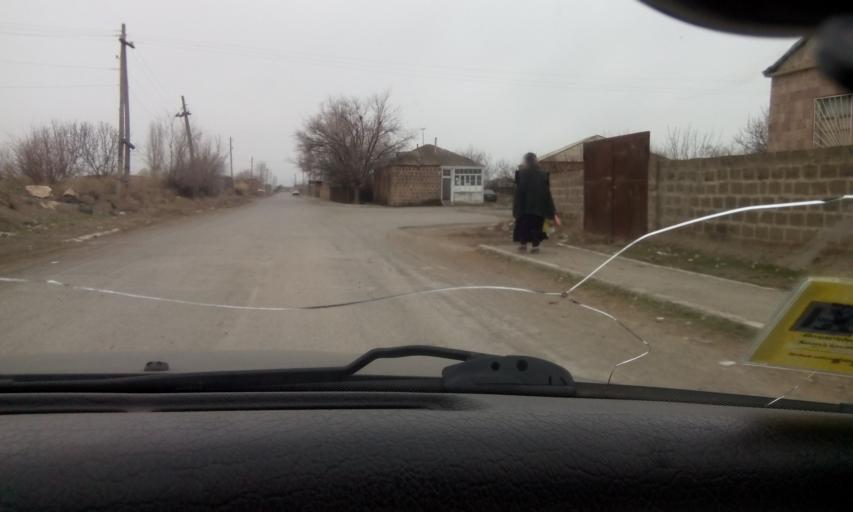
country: AM
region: Armavir
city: Lukashin
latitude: 40.1850
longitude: 43.9808
